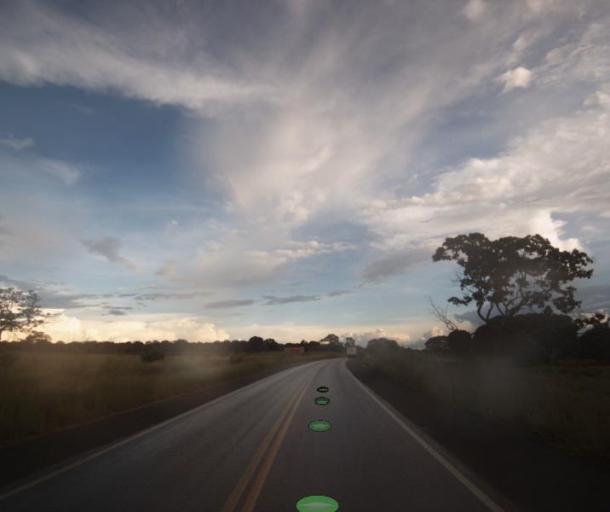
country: BR
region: Goias
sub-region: Uruacu
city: Uruacu
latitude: -14.0101
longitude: -49.0854
